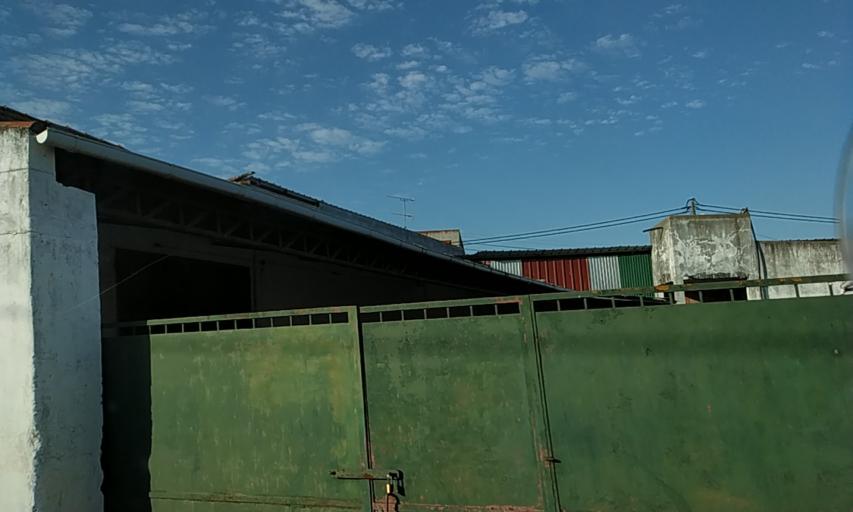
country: PT
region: Santarem
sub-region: Santarem
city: Santarem
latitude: 39.3359
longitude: -8.6624
